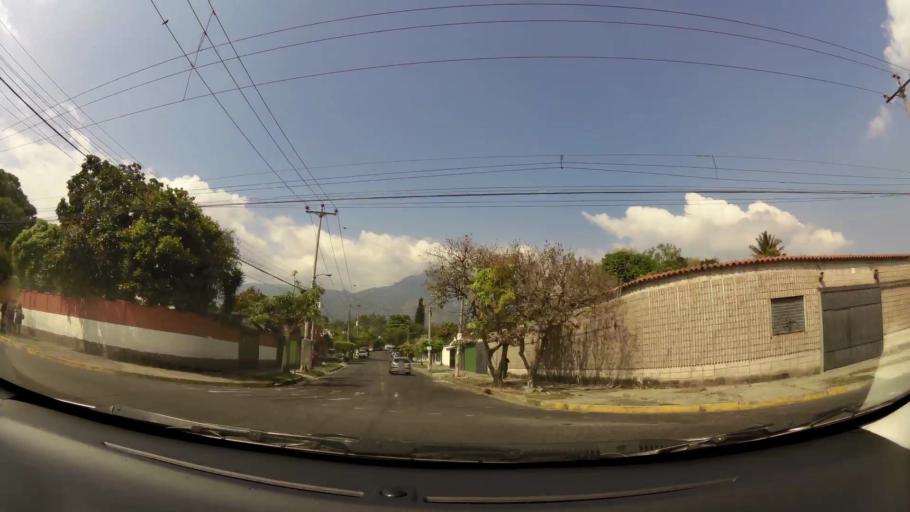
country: SV
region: San Salvador
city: Mejicanos
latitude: 13.7080
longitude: -89.2173
